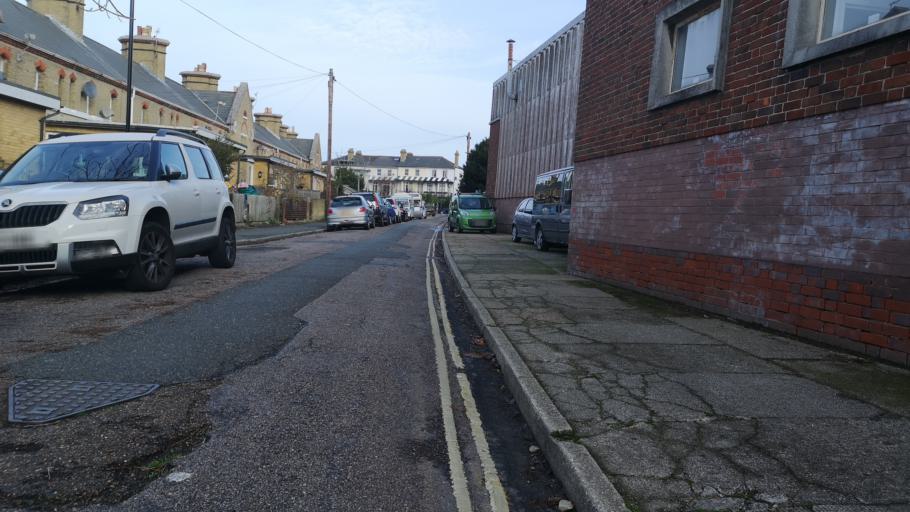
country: GB
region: England
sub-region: Isle of Wight
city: East Cowes
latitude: 50.7613
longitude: -1.2885
